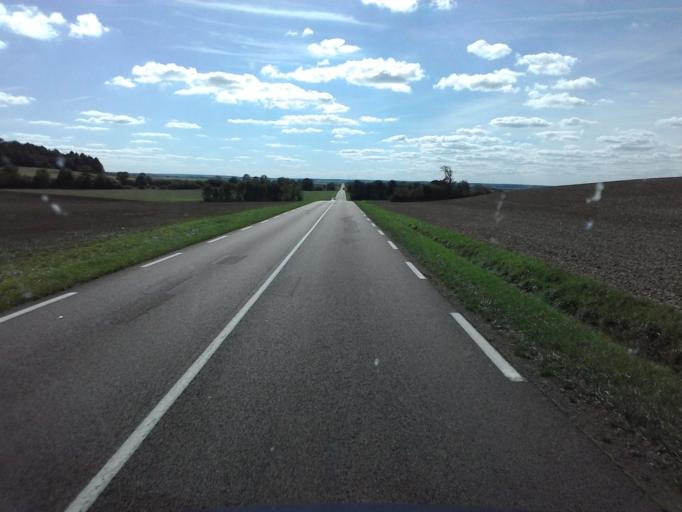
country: FR
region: Bourgogne
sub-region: Departement de la Cote-d'Or
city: Chatillon-sur-Seine
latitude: 47.8979
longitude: 4.6135
